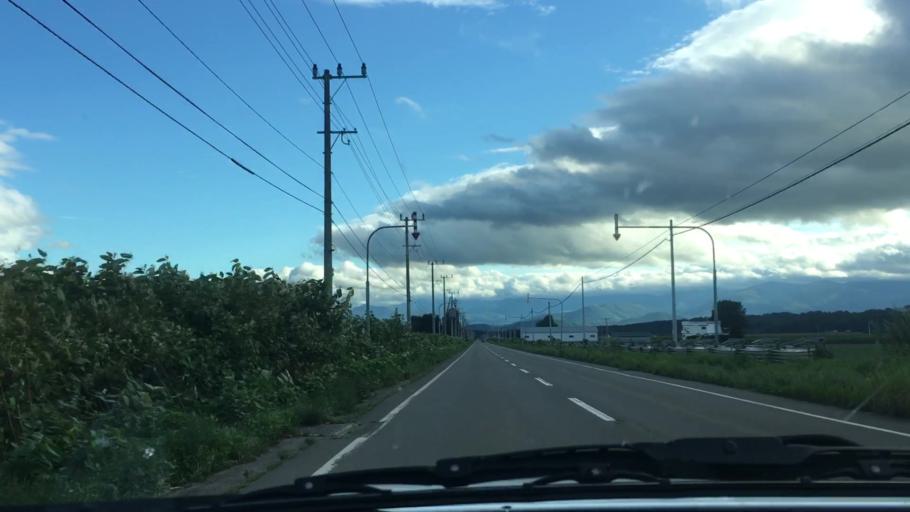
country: JP
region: Hokkaido
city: Otofuke
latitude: 43.1568
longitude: 142.9027
